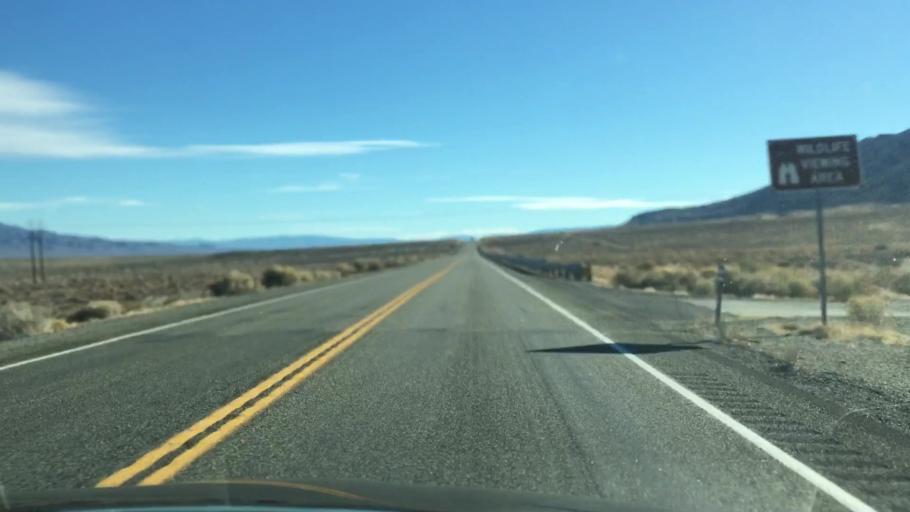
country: US
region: Nevada
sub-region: Mineral County
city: Hawthorne
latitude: 38.8131
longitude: -118.7660
